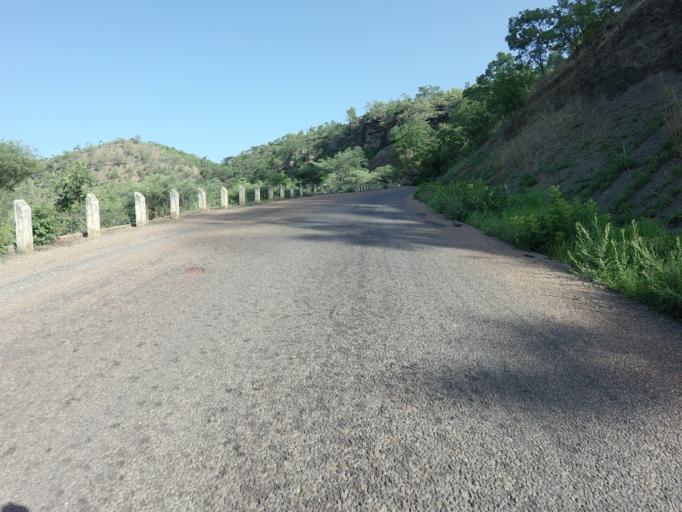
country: GH
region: Upper East
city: Bawku
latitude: 10.6442
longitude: -0.1965
